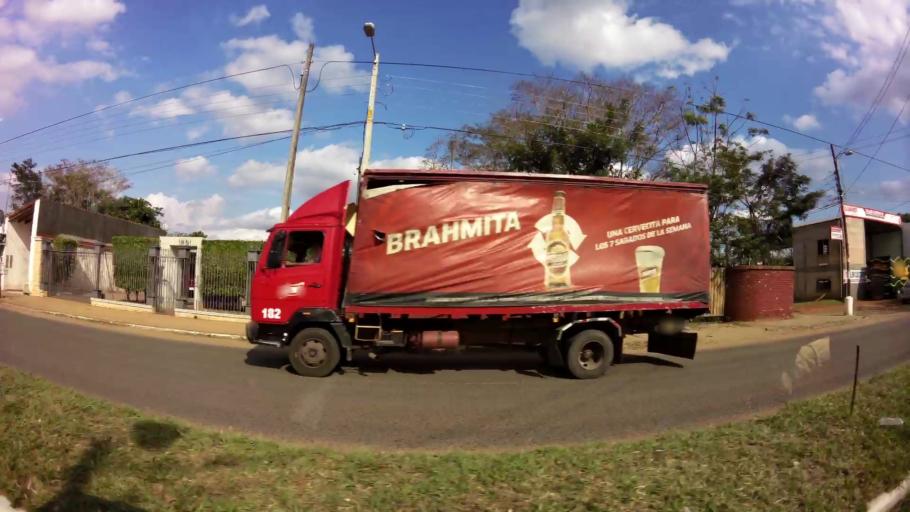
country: PY
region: Central
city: Fernando de la Mora
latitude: -25.3426
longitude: -57.5407
